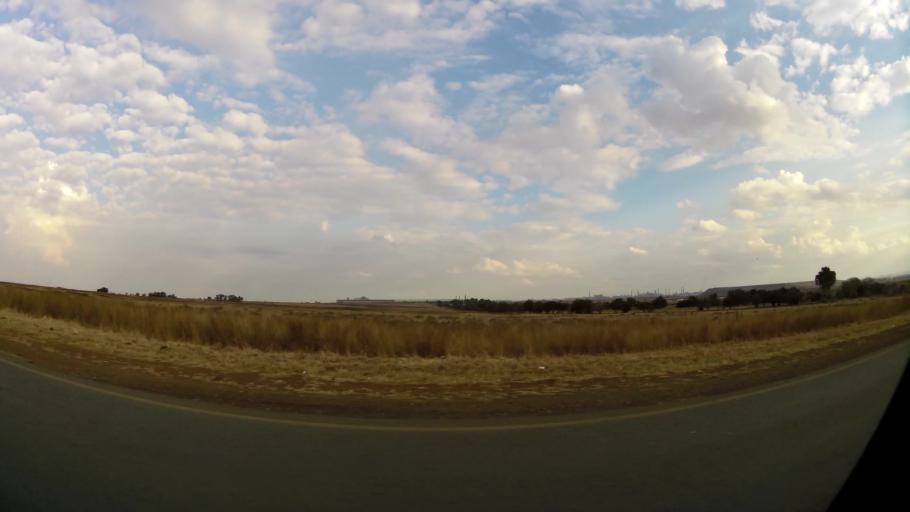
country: ZA
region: Gauteng
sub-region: Sedibeng District Municipality
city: Vanderbijlpark
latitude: -26.6187
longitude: 27.8366
